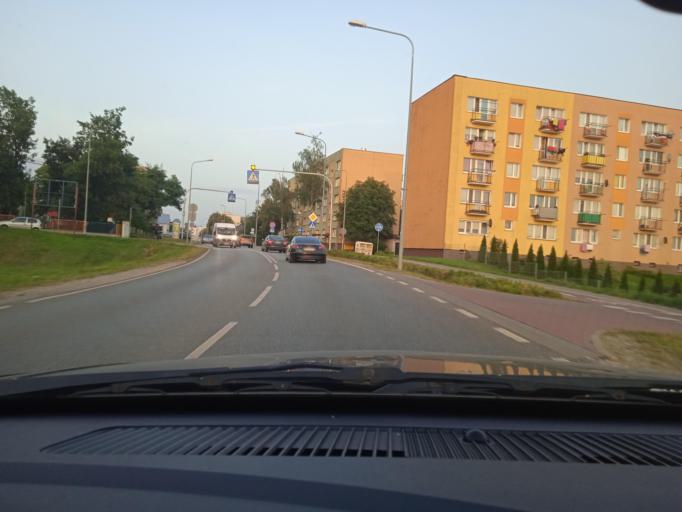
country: PL
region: Masovian Voivodeship
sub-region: Powiat nowodworski
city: Nowy Dwor Mazowiecki
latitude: 52.4291
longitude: 20.7080
